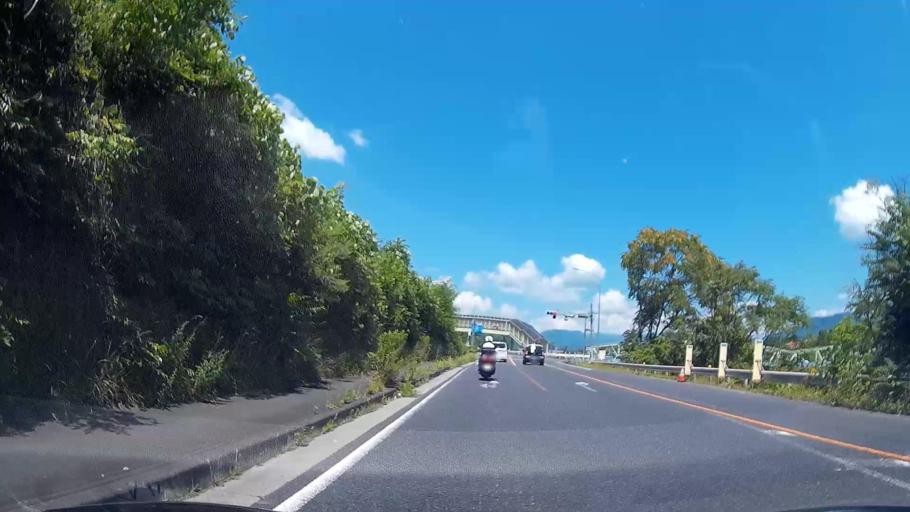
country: JP
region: Gunma
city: Numata
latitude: 36.6313
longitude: 139.0375
